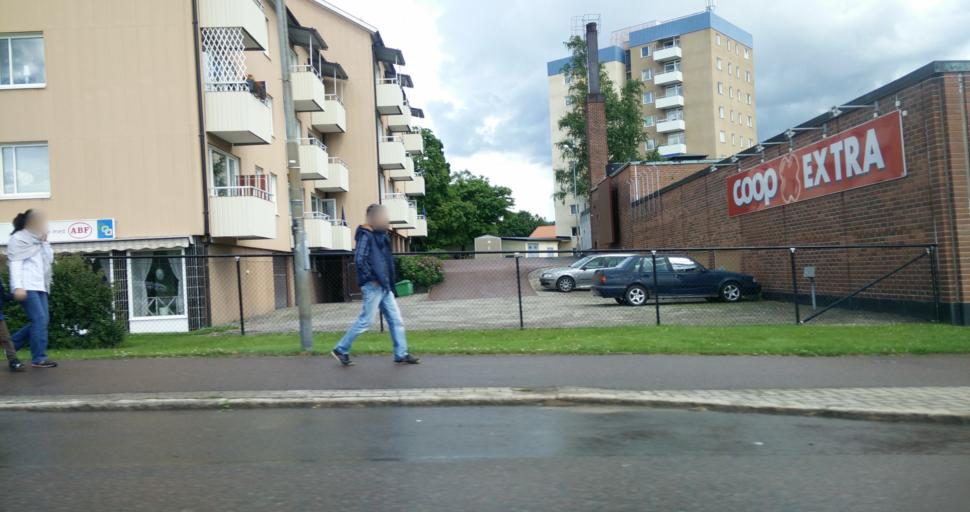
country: SE
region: Vaermland
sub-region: Hagfors Kommun
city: Hagfors
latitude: 60.0354
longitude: 13.6949
